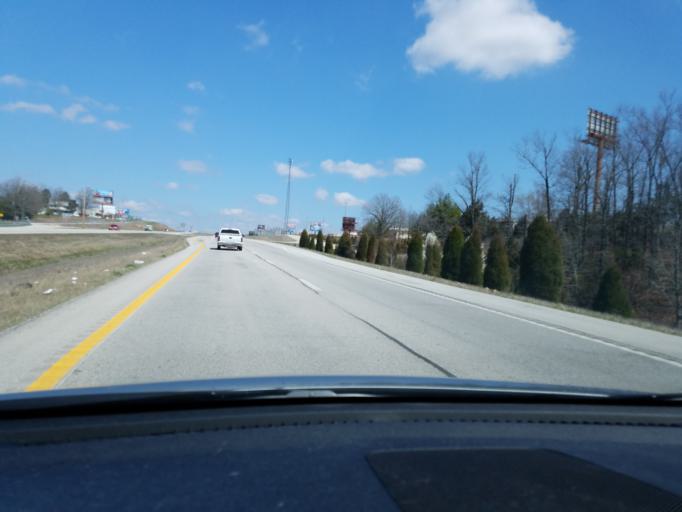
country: US
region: Missouri
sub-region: Taney County
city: Merriam Woods
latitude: 36.8029
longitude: -93.2260
